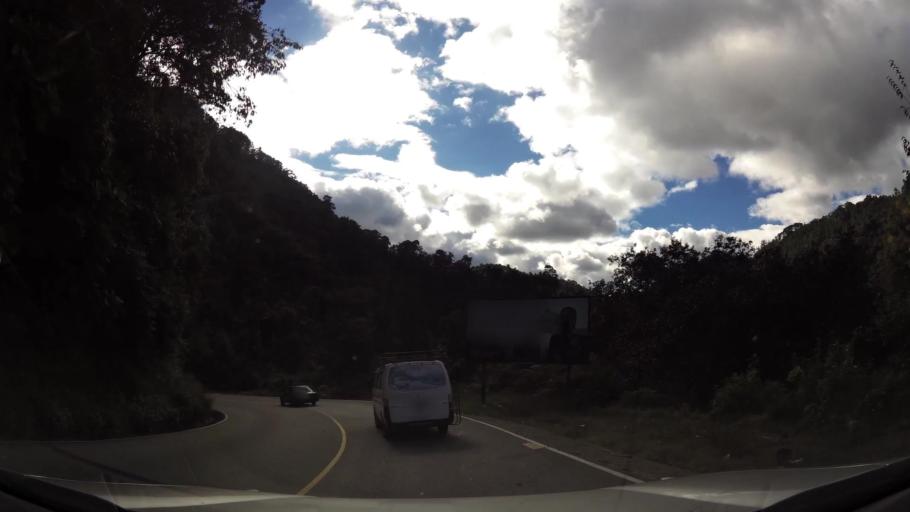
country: GT
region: Quiche
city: Chichicastenango
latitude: 14.9188
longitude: -91.1033
